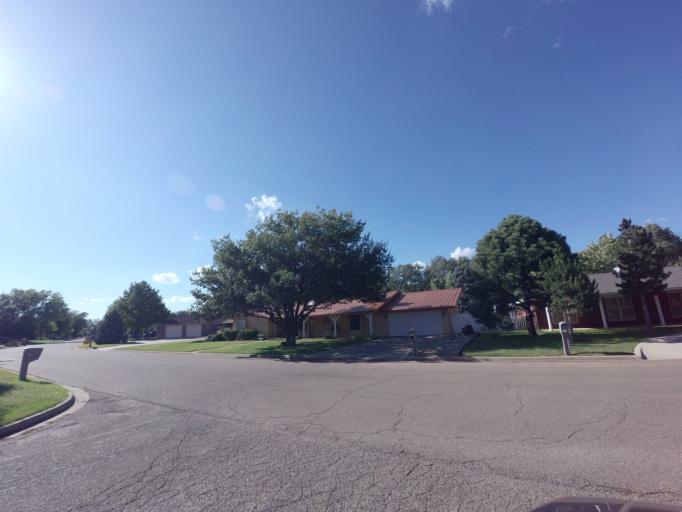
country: US
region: New Mexico
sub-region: Curry County
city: Clovis
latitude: 34.4384
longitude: -103.1815
